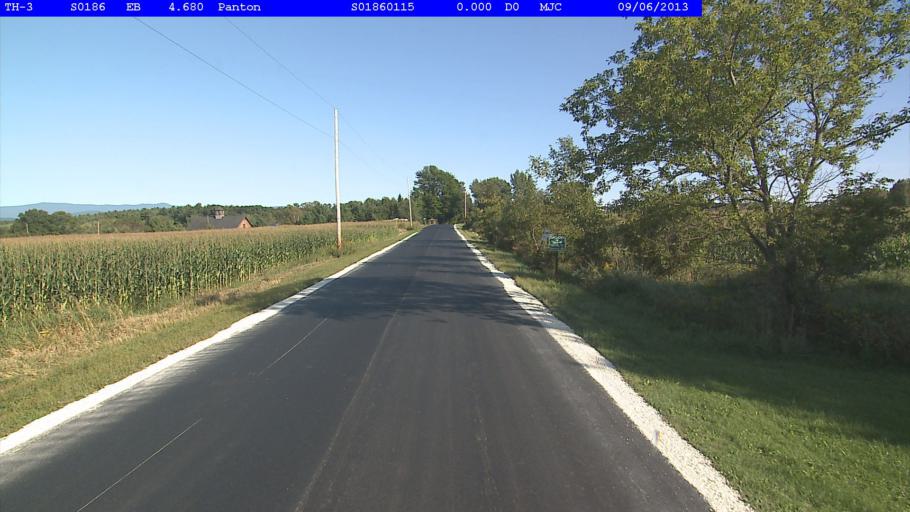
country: US
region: Vermont
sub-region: Addison County
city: Vergennes
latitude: 44.1629
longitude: -73.2930
